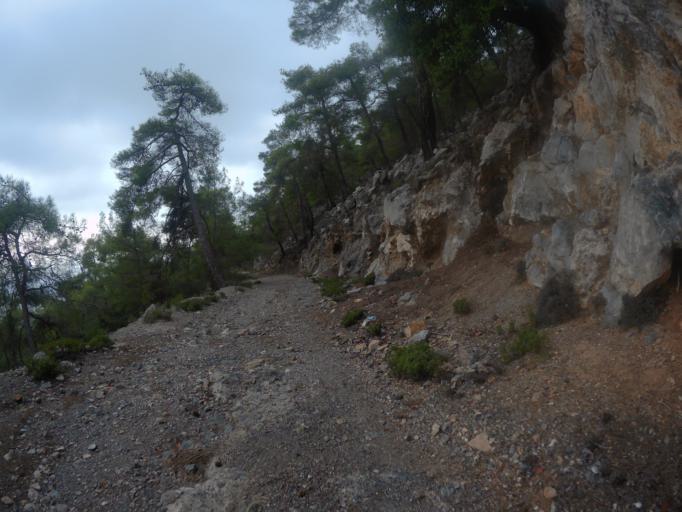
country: CY
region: Ammochostos
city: Lefkonoiko
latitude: 35.2958
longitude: 33.5627
